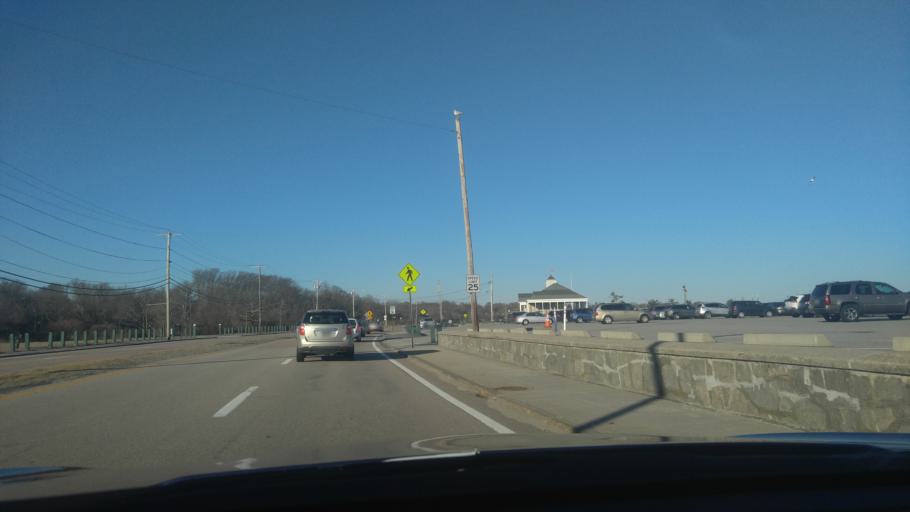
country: US
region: Rhode Island
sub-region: Washington County
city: Narragansett Pier
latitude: 41.4342
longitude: -71.4568
